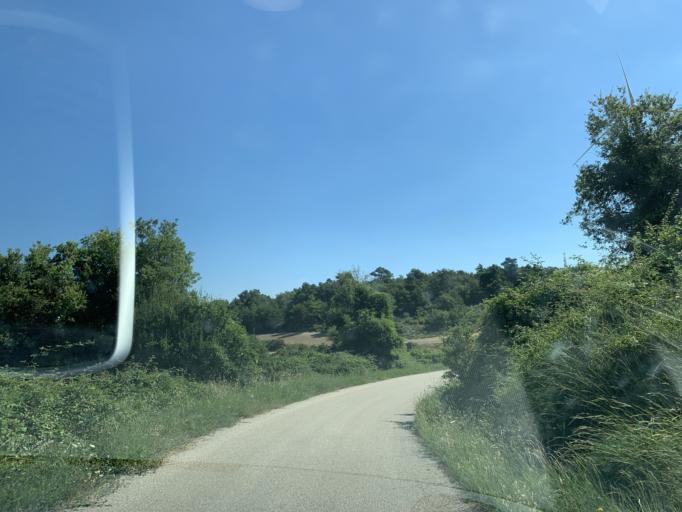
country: ES
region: Catalonia
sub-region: Provincia de Tarragona
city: Conesa
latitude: 41.5394
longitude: 1.2851
